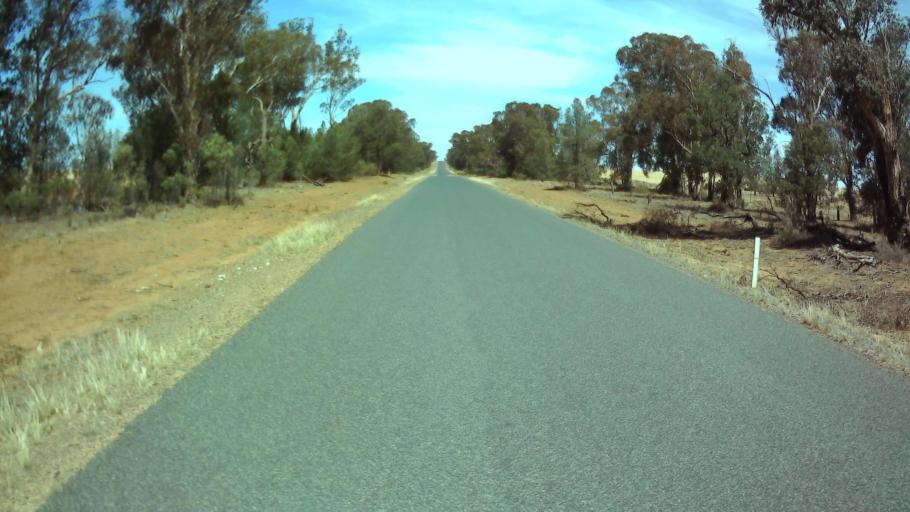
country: AU
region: New South Wales
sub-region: Weddin
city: Grenfell
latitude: -33.8955
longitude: 147.7492
